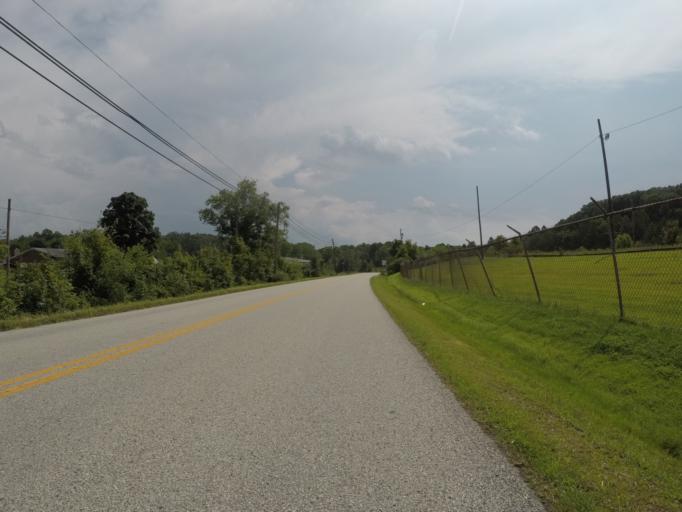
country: US
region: Kentucky
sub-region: Boyd County
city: Ironville
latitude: 38.4455
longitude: -82.7000
